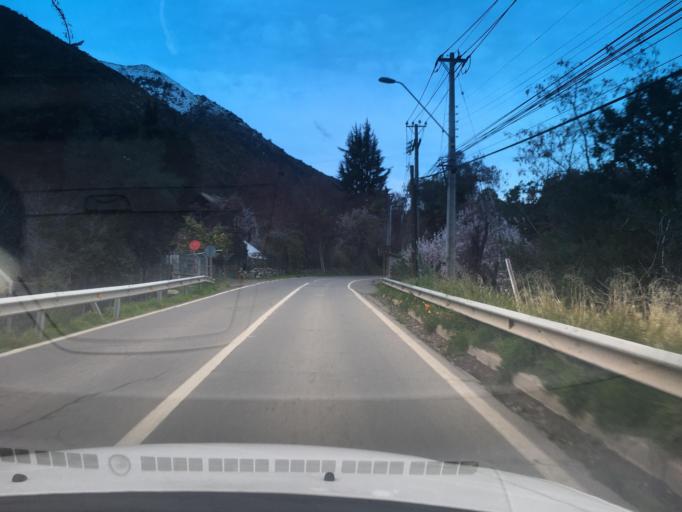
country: CL
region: Santiago Metropolitan
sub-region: Provincia de Cordillera
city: Puente Alto
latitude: -33.5756
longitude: -70.4463
